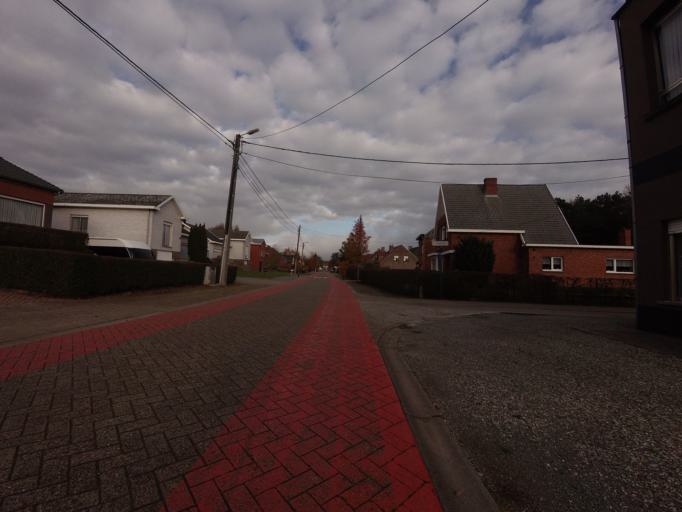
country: BE
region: Flanders
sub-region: Provincie Antwerpen
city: Bonheiden
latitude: 51.0342
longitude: 4.5862
